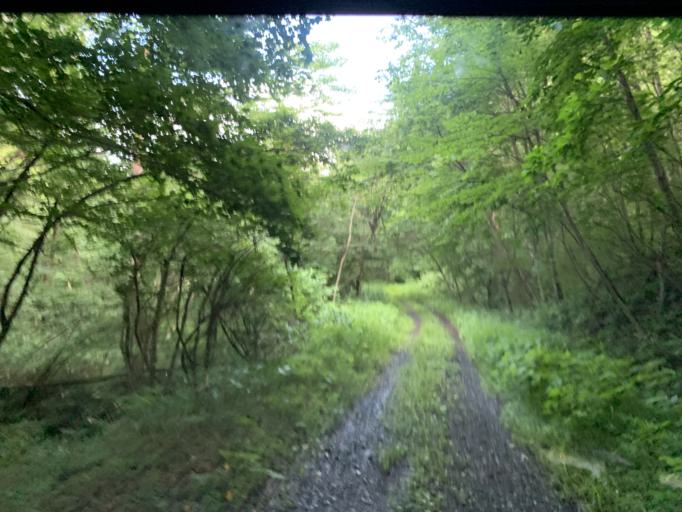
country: JP
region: Iwate
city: Ichinoseki
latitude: 38.9095
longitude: 140.9481
